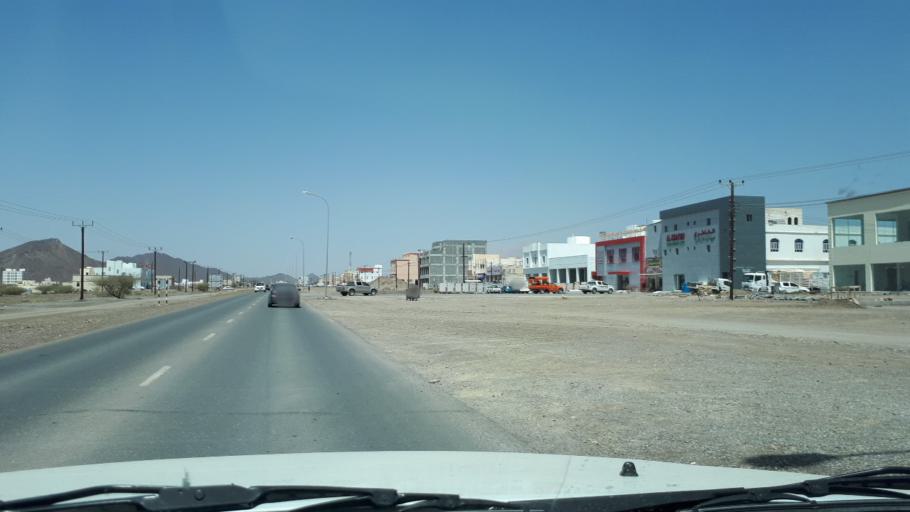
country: OM
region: Muhafazat ad Dakhiliyah
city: Bahla'
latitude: 22.9475
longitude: 57.2700
